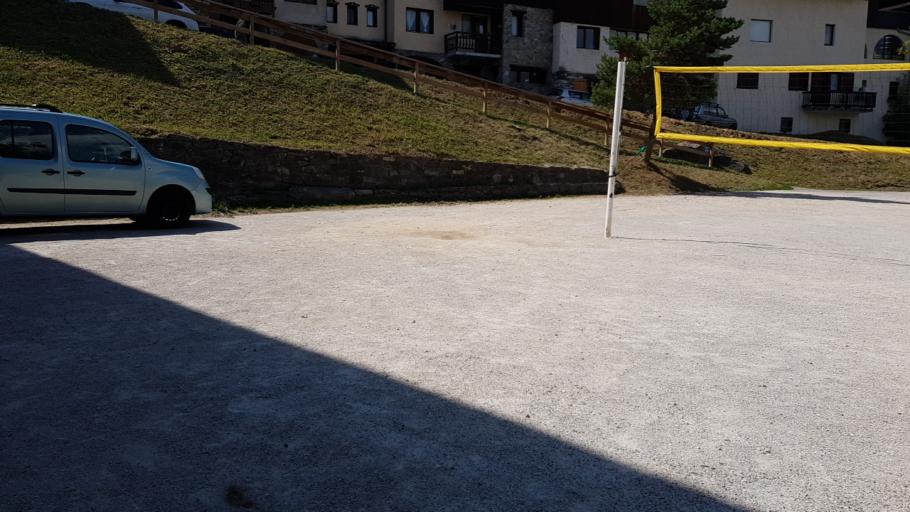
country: FR
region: Rhone-Alpes
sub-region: Departement de la Savoie
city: Belle-Plagne
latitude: 45.5606
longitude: 6.7358
